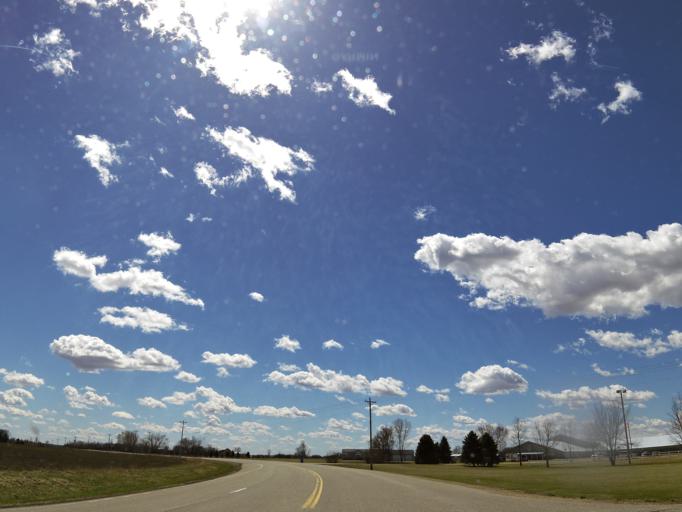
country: US
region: Minnesota
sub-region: Washington County
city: Cottage Grove
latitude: 44.7385
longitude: -92.9535
